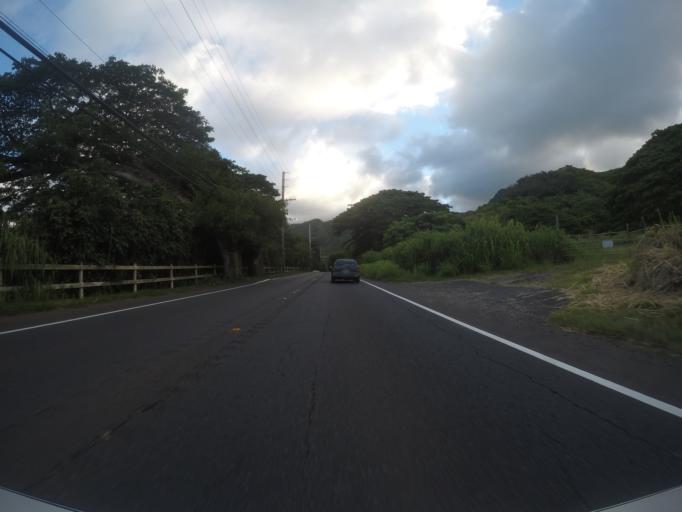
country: US
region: Hawaii
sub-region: Honolulu County
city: Ka'a'awa
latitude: 21.5118
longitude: -157.8508
